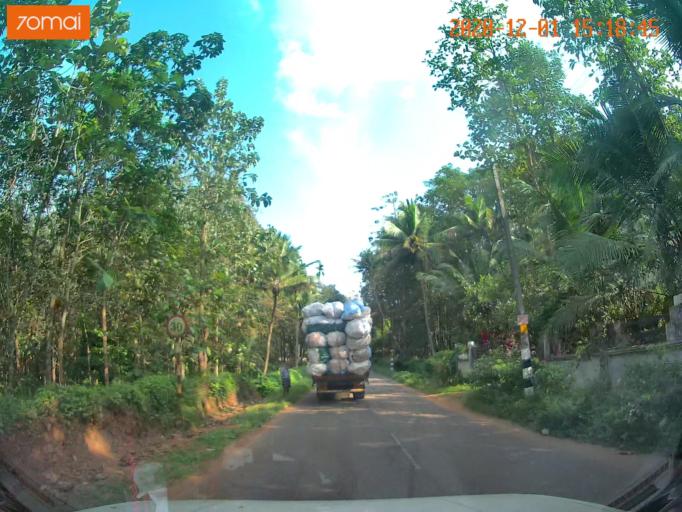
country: IN
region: Kerala
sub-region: Ernakulam
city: Ramamangalam
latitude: 9.9360
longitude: 76.5328
